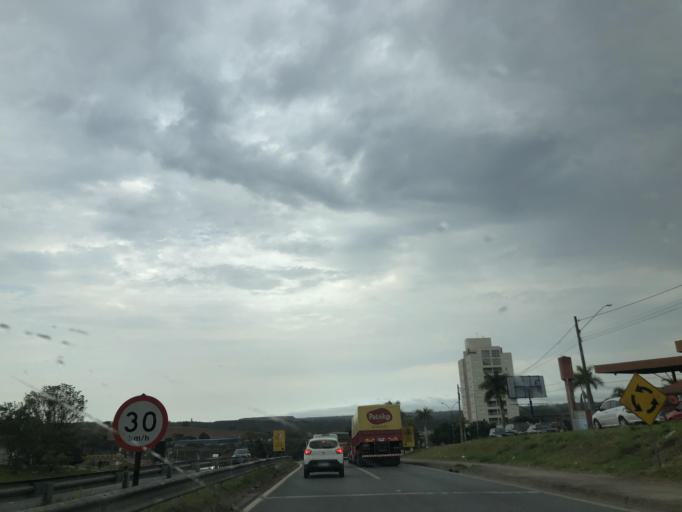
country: BR
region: Sao Paulo
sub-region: Salto De Pirapora
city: Salto de Pirapora
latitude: -23.6407
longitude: -47.5770
